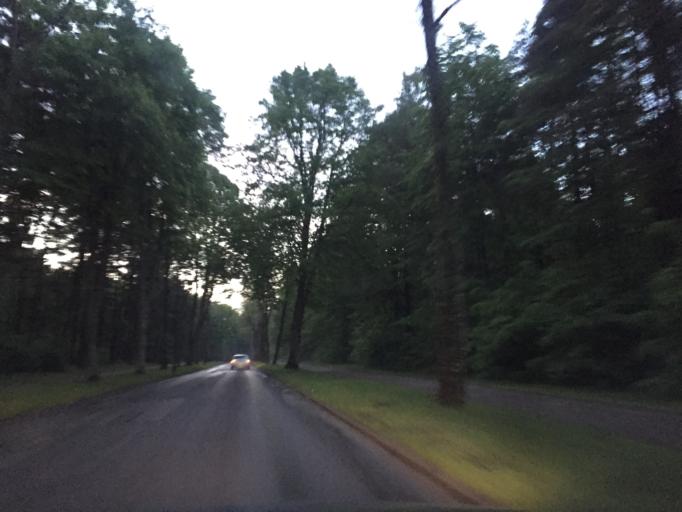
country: LT
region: Klaipedos apskritis
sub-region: Klaipeda
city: Palanga
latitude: 55.9005
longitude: 21.0617
